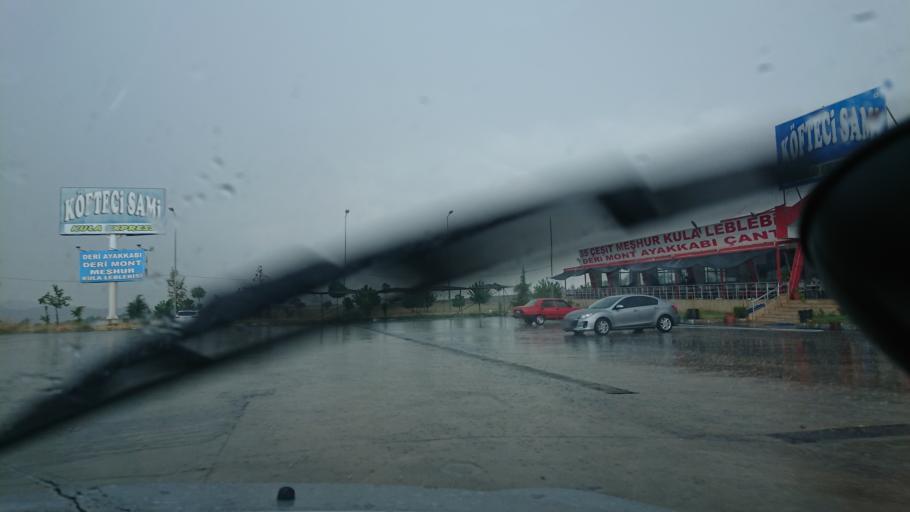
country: TR
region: Manisa
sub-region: Kula
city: Kula
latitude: 38.5645
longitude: 28.5895
